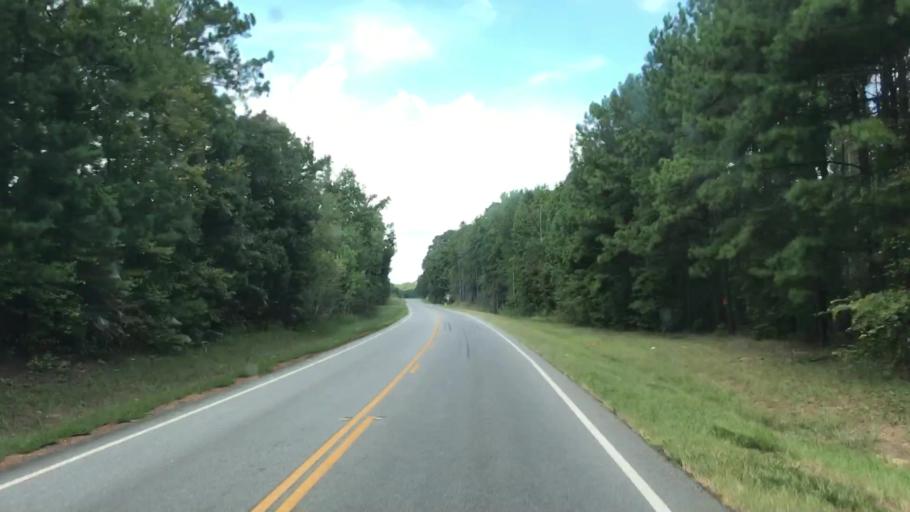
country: US
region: Georgia
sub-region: Greene County
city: Greensboro
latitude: 33.7010
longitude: -83.2824
